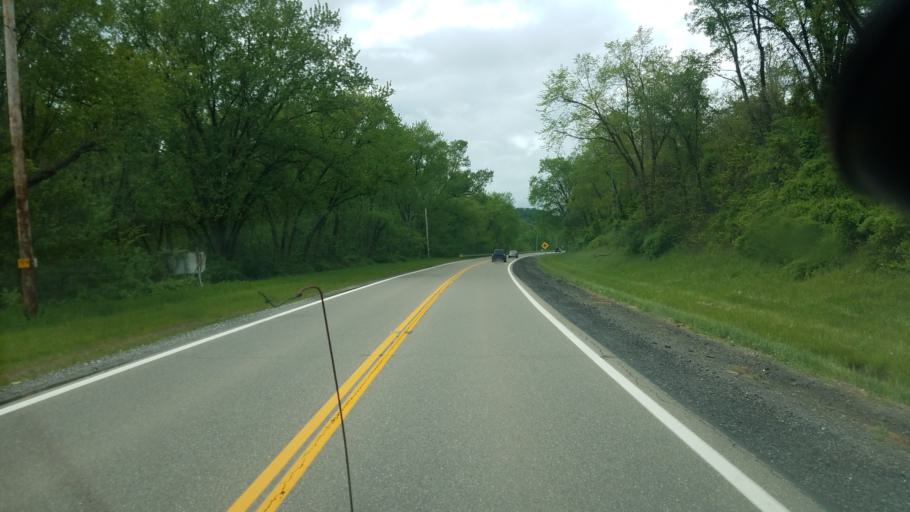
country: US
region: Ohio
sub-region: Harrison County
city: Cadiz
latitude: 40.3119
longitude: -81.1117
